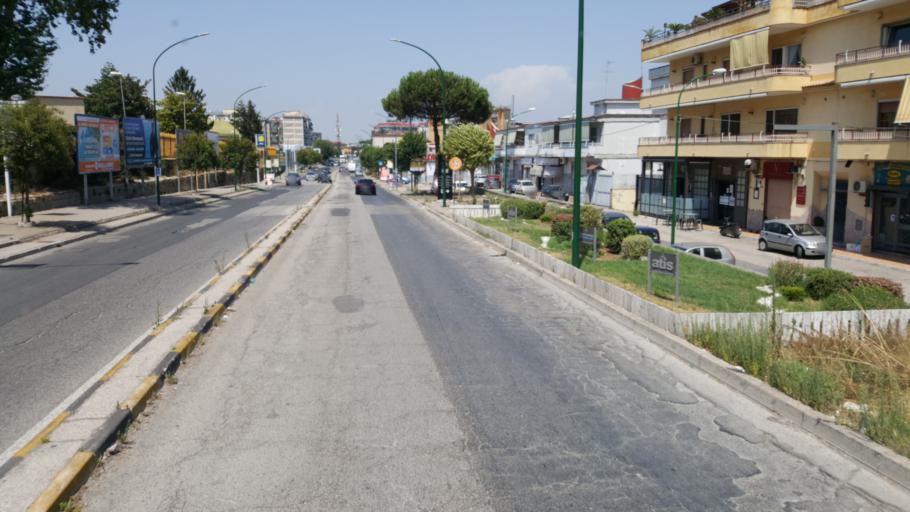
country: IT
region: Campania
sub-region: Provincia di Napoli
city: Arpino
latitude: 40.8850
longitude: 14.3202
